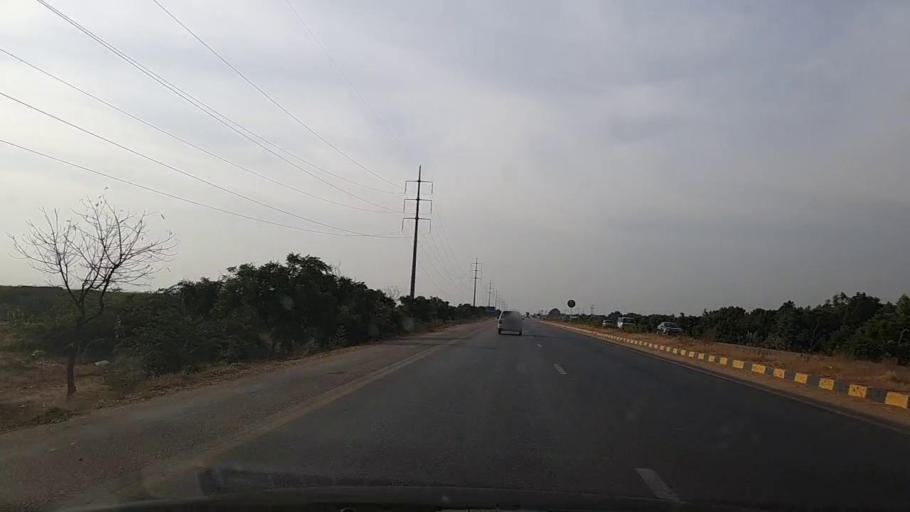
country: PK
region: Sindh
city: Gharo
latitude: 24.8272
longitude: 67.4710
